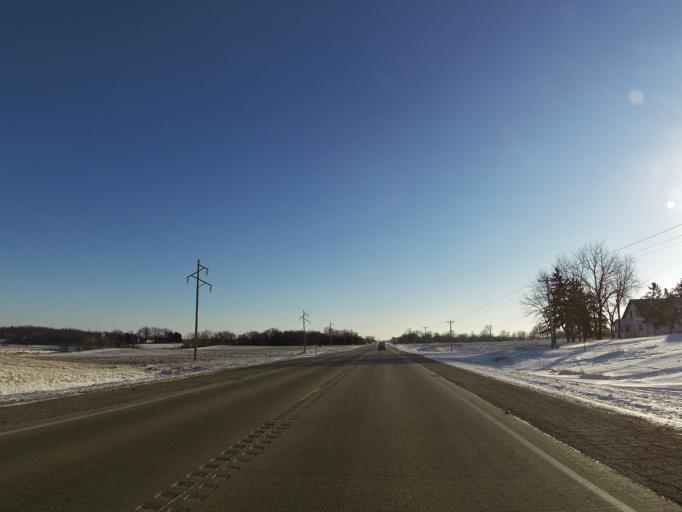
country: US
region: Minnesota
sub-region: Le Sueur County
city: New Prague
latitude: 44.5074
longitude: -93.5857
